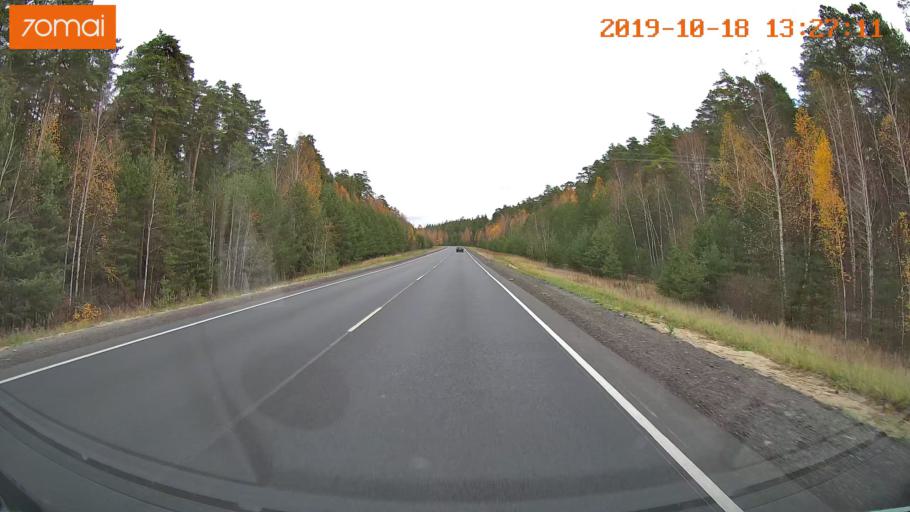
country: RU
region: Rjazan
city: Solotcha
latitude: 54.7612
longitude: 39.8502
